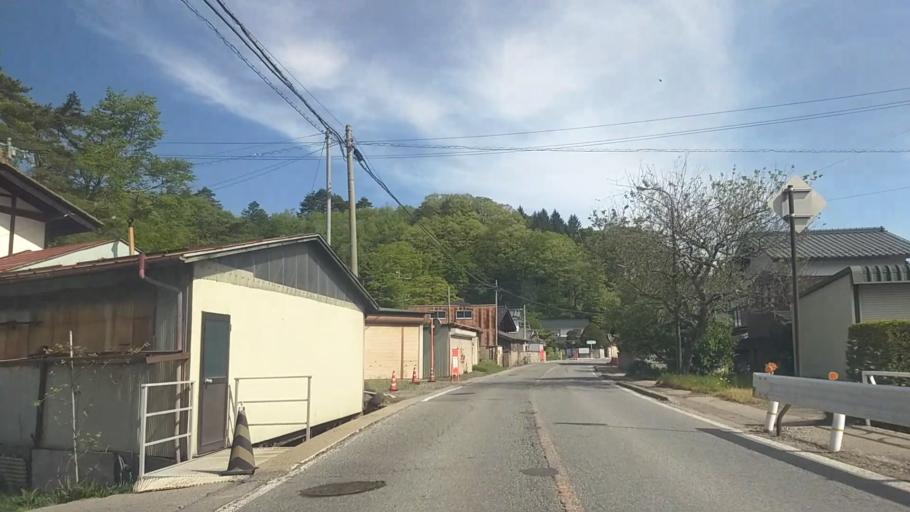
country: JP
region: Nagano
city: Saku
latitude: 36.0389
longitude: 138.4720
